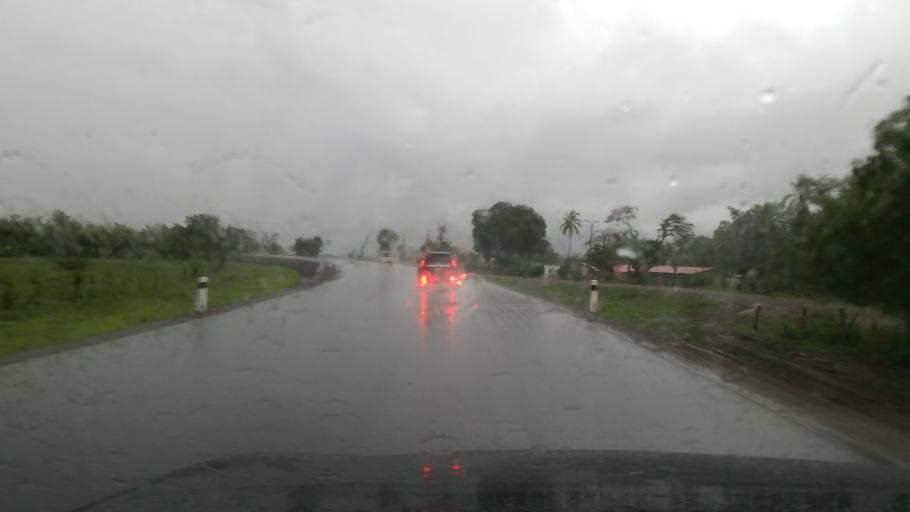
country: NI
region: Chinandega
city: Chichigalpa
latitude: 12.7838
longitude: -86.9364
